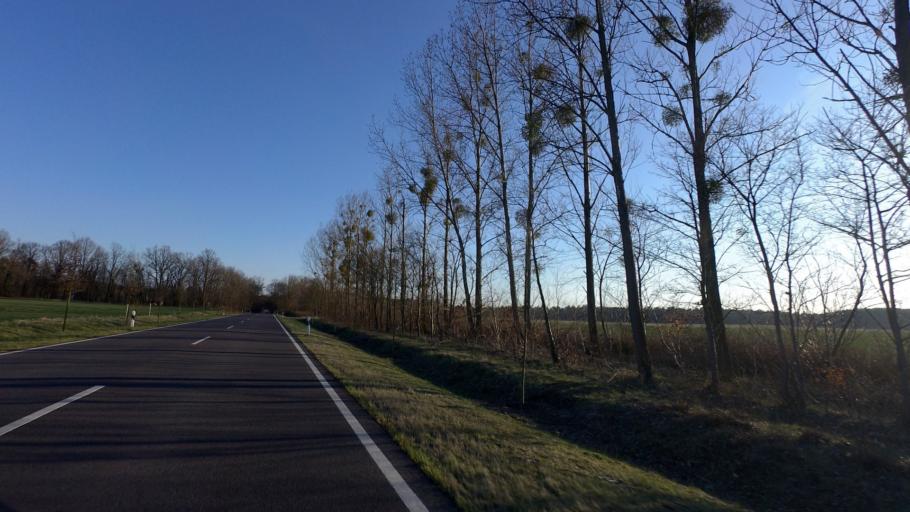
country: DE
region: Brandenburg
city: Werftpfuhl
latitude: 52.6874
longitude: 13.8359
